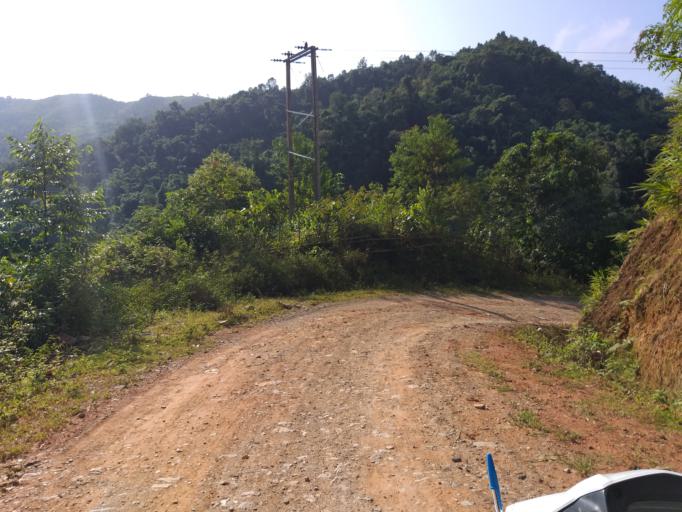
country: LA
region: Phongsali
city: Khoa
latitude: 21.1964
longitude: 102.6647
